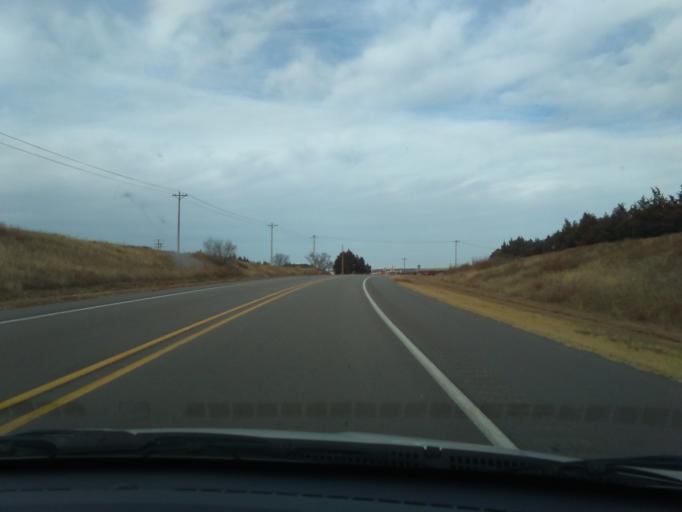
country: US
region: Nebraska
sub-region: Dundy County
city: Benkelman
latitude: 40.0520
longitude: -101.5435
